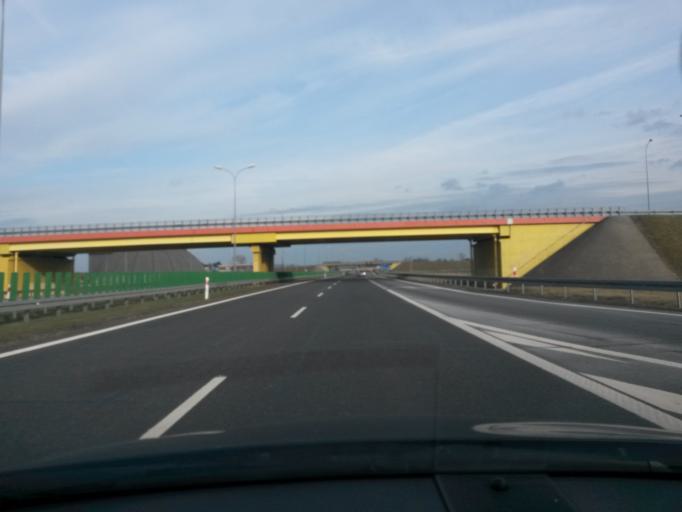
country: PL
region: Lodz Voivodeship
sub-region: Powiat poddebicki
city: Wartkowice
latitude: 51.9948
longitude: 19.0385
